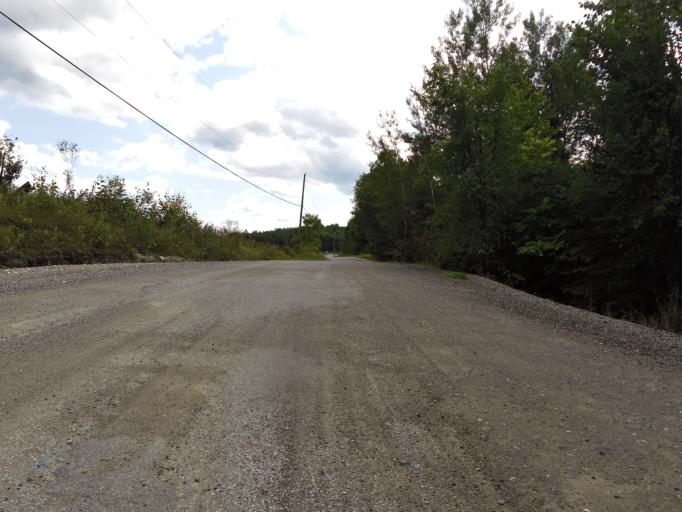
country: CA
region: Quebec
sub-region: Outaouais
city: Wakefield
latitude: 45.8073
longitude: -75.9850
